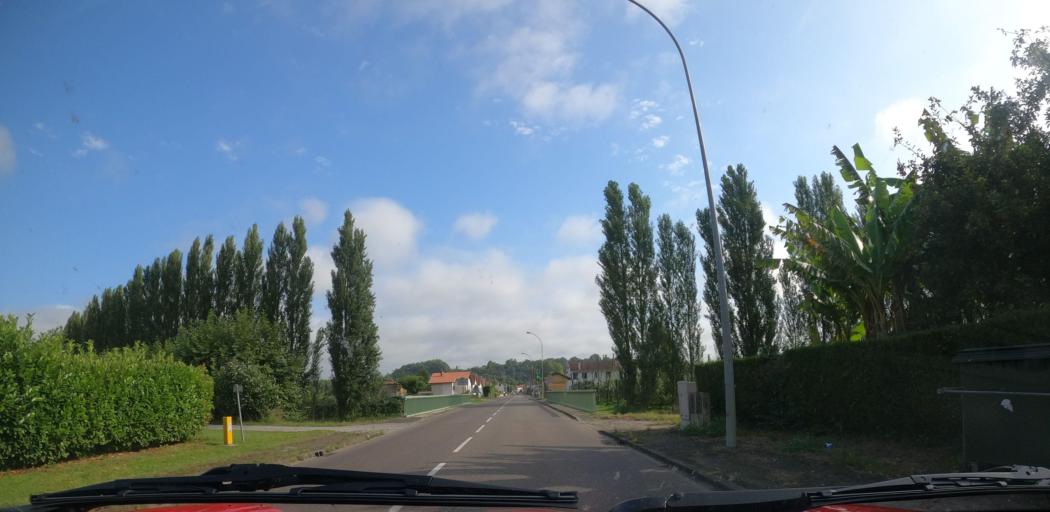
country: FR
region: Aquitaine
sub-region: Departement des Landes
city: Peyrehorade
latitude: 43.5384
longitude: -1.1076
